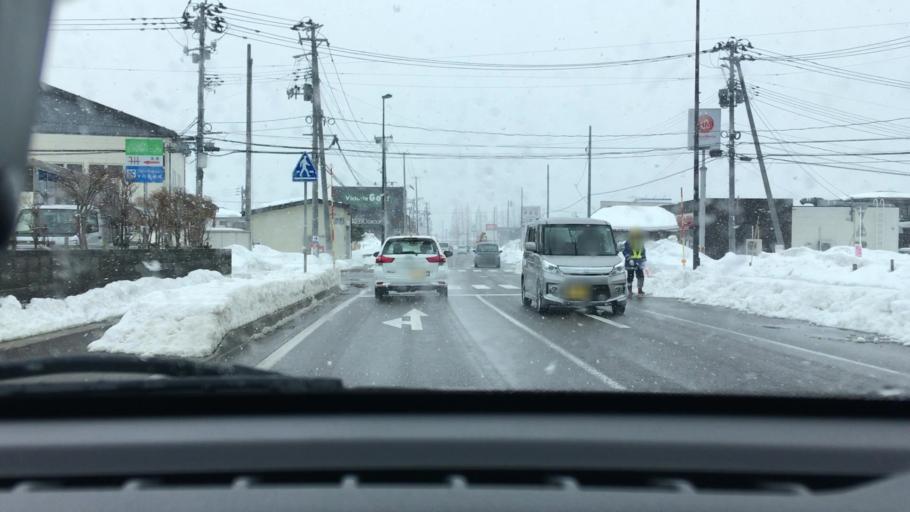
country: JP
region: Niigata
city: Joetsu
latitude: 37.1610
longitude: 138.2533
